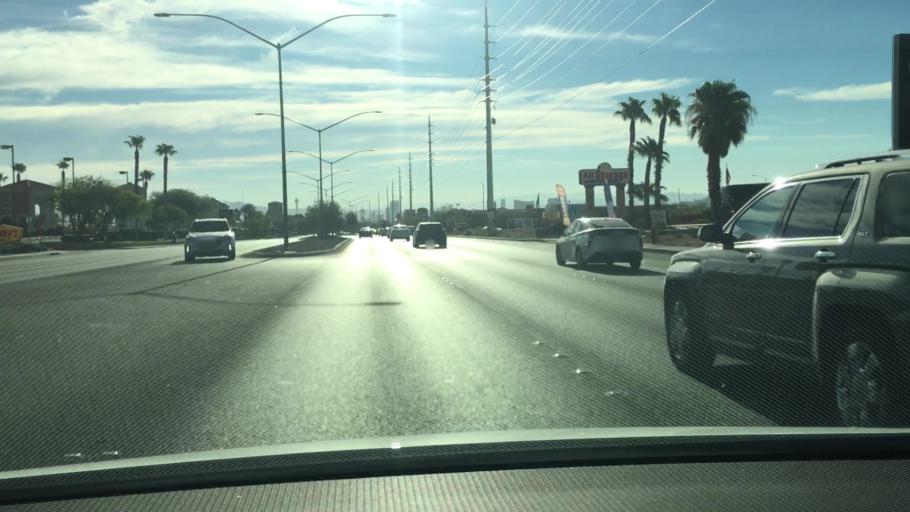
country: US
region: Nevada
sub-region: Clark County
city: Spring Valley
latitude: 36.1438
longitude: -115.2673
